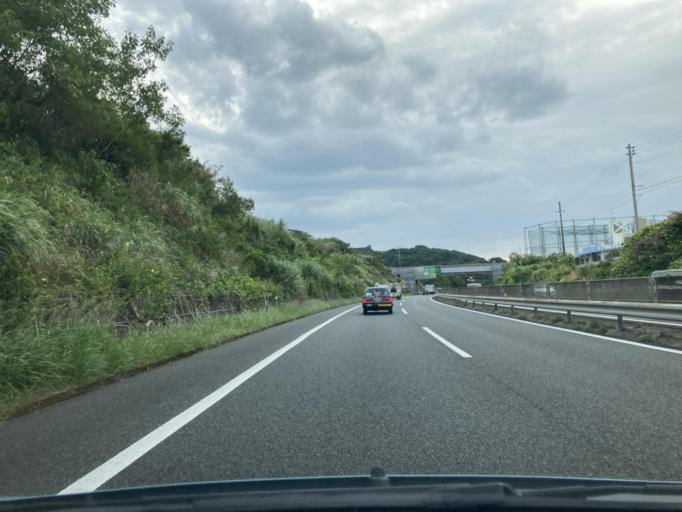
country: JP
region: Okinawa
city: Ginowan
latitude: 26.2503
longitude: 127.7594
